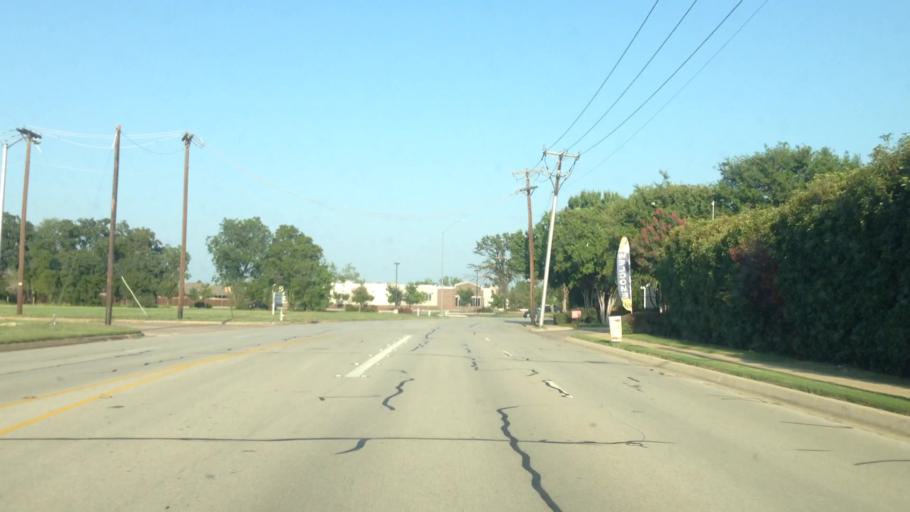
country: US
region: Texas
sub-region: Tarrant County
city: Pantego
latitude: 32.7536
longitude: -97.1759
